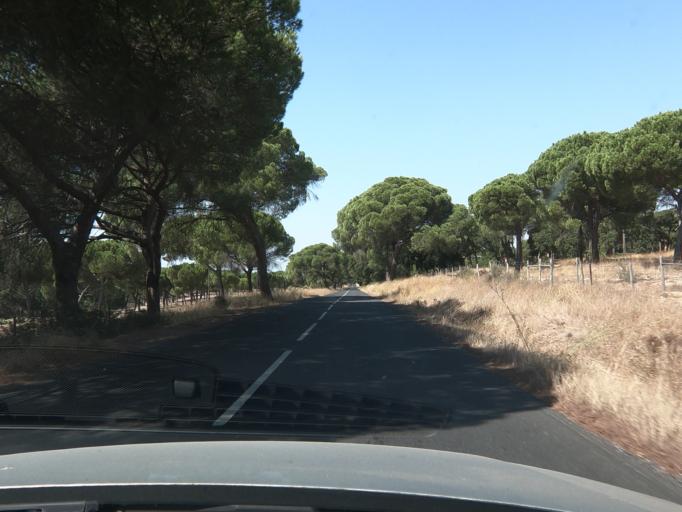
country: PT
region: Setubal
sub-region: Alcacer do Sal
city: Alcacer do Sal
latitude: 38.3487
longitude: -8.4619
